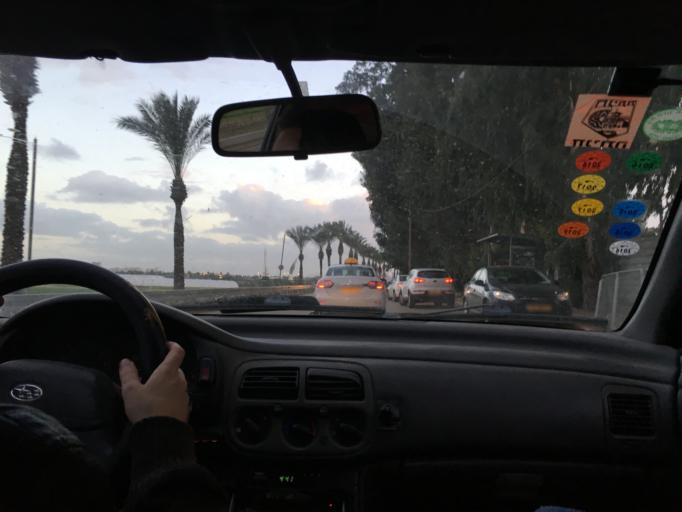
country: IL
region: Tel Aviv
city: Ramat HaSharon
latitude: 32.1424
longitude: 34.8174
